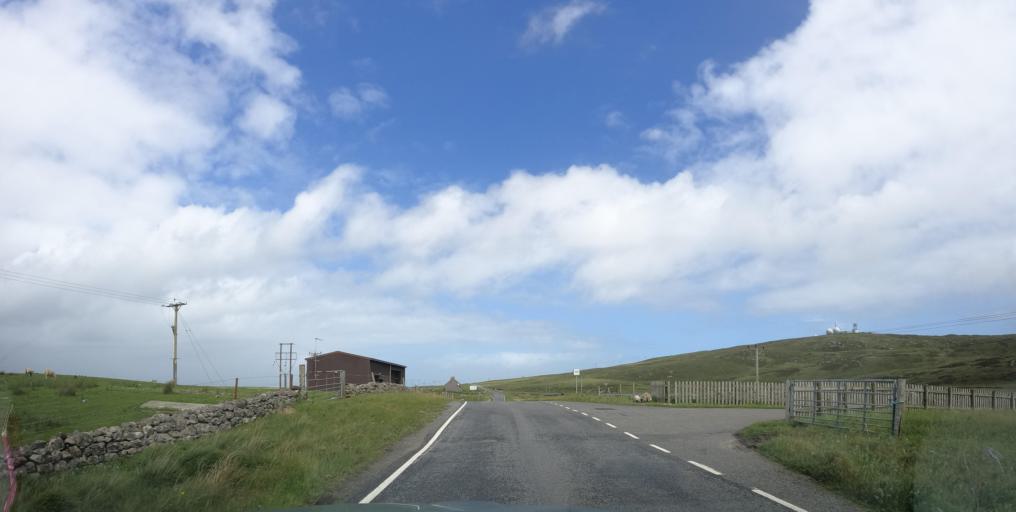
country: GB
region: Scotland
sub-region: Eilean Siar
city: Isle of South Uist
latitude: 57.3360
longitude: -7.3638
